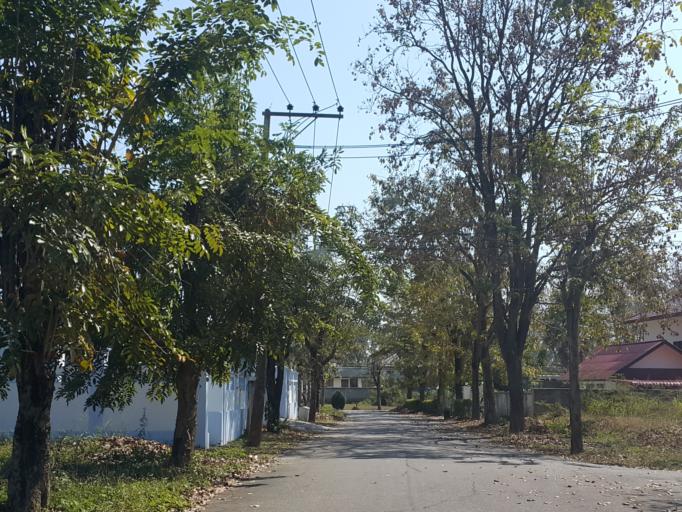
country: TH
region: Chiang Mai
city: Chiang Mai
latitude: 18.7322
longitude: 98.9705
